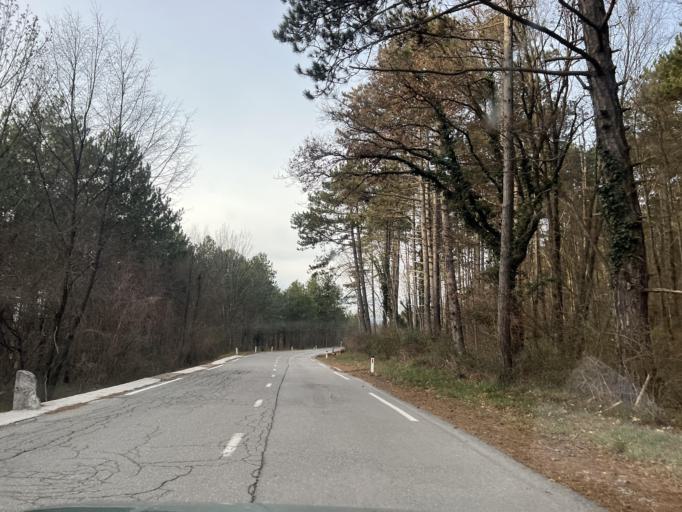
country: SI
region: Nova Gorica
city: Sempas
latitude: 45.9755
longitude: 13.7185
